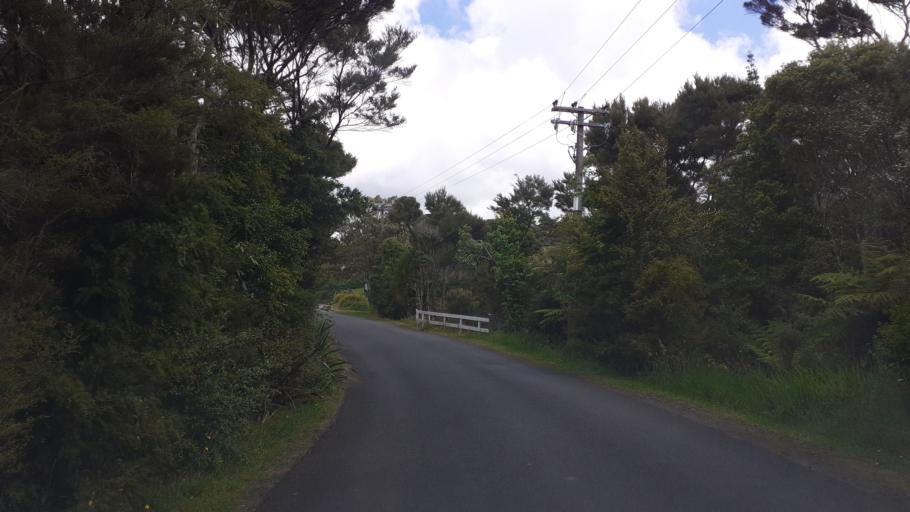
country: NZ
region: Northland
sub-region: Far North District
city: Paihia
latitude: -35.3118
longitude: 174.1133
